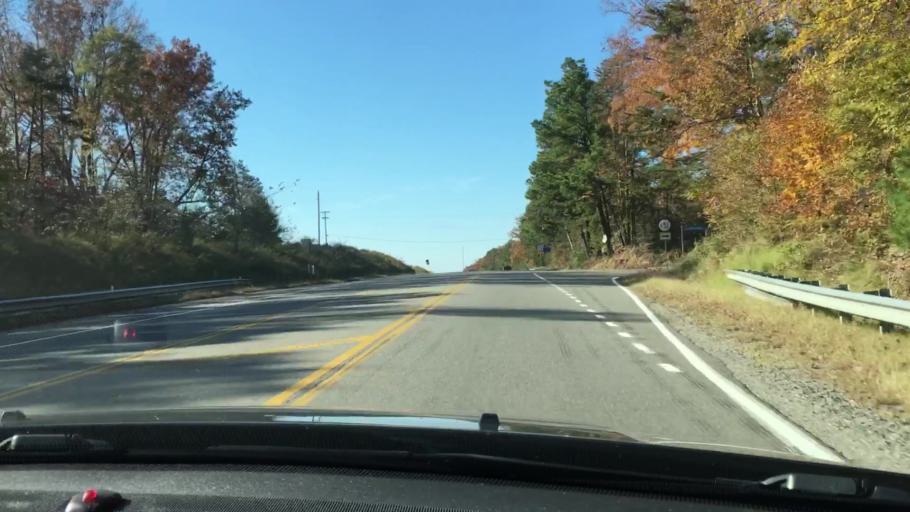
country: US
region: Virginia
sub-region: Hanover County
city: Hanover
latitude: 37.8499
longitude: -77.4060
